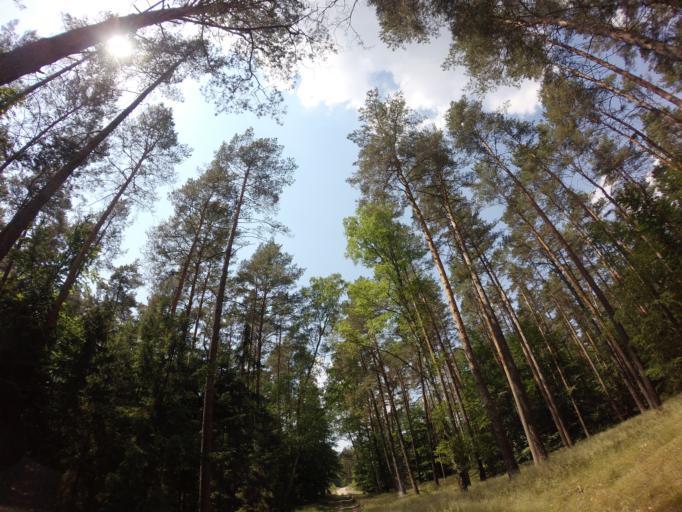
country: PL
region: West Pomeranian Voivodeship
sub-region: Powiat choszczenski
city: Bierzwnik
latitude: 53.0821
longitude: 15.7169
